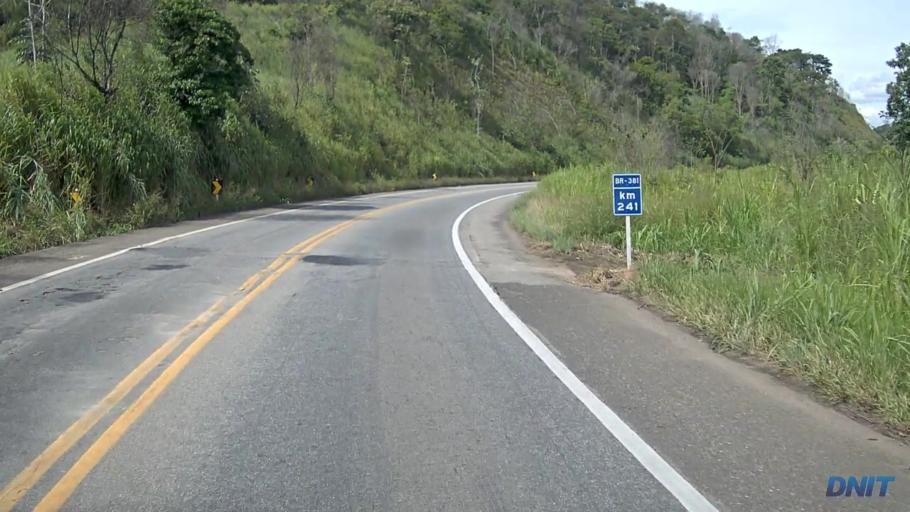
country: BR
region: Minas Gerais
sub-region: Ipaba
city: Ipaba
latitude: -19.3854
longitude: -42.4751
